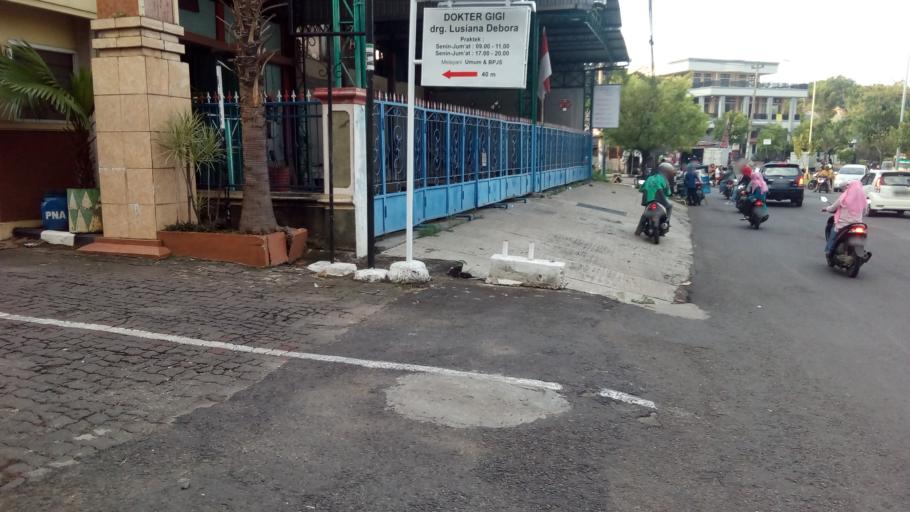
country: ID
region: Central Java
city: Semarang
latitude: -6.9933
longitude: 110.3511
